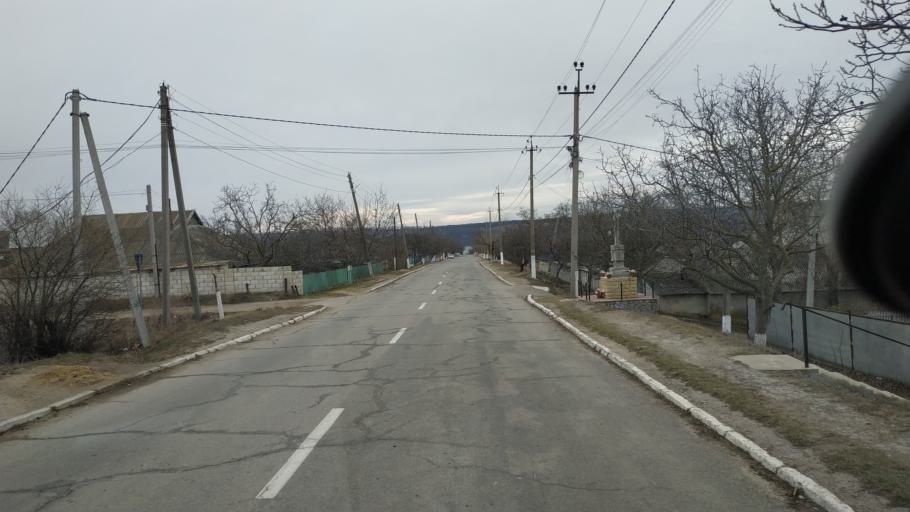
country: MD
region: Telenesti
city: Cocieri
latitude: 47.3517
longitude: 29.1170
